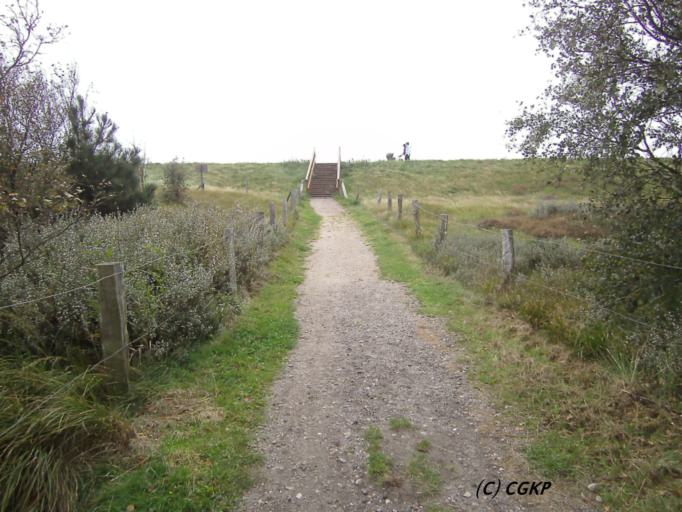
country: DE
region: Schleswig-Holstein
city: Sankt Peter-Ording
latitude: 54.2857
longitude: 8.6560
